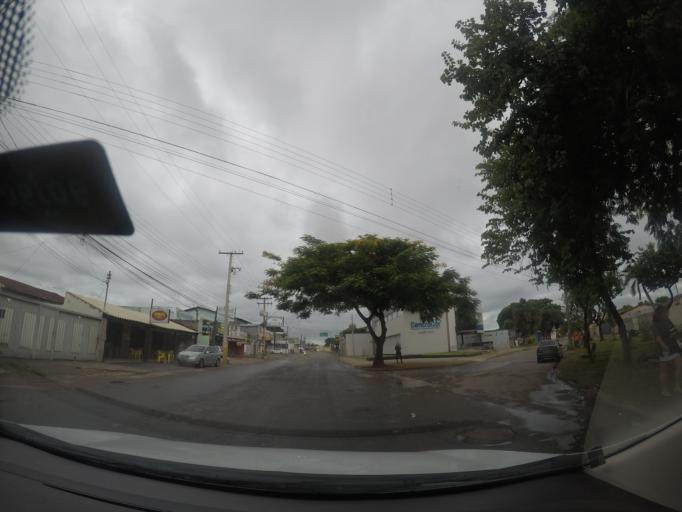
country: BR
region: Goias
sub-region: Goiania
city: Goiania
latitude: -16.7148
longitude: -49.3073
